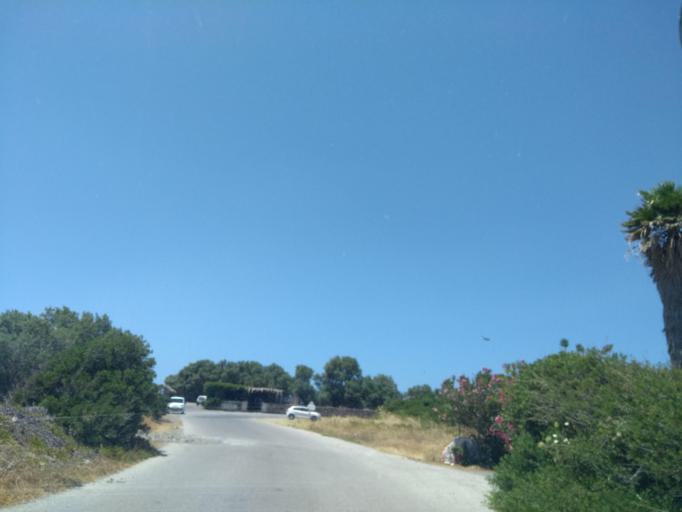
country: GR
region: Crete
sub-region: Nomos Chanias
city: Vryses
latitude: 35.3593
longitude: 23.5320
